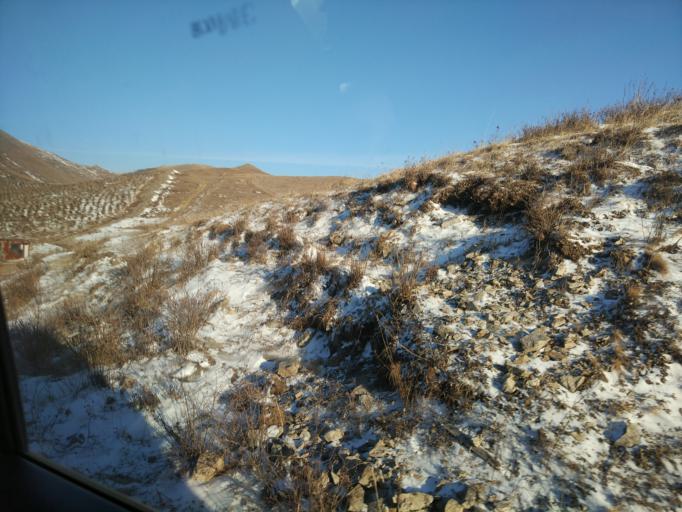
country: CN
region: Hebei
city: Xiwanzi
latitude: 40.8757
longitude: 115.4542
